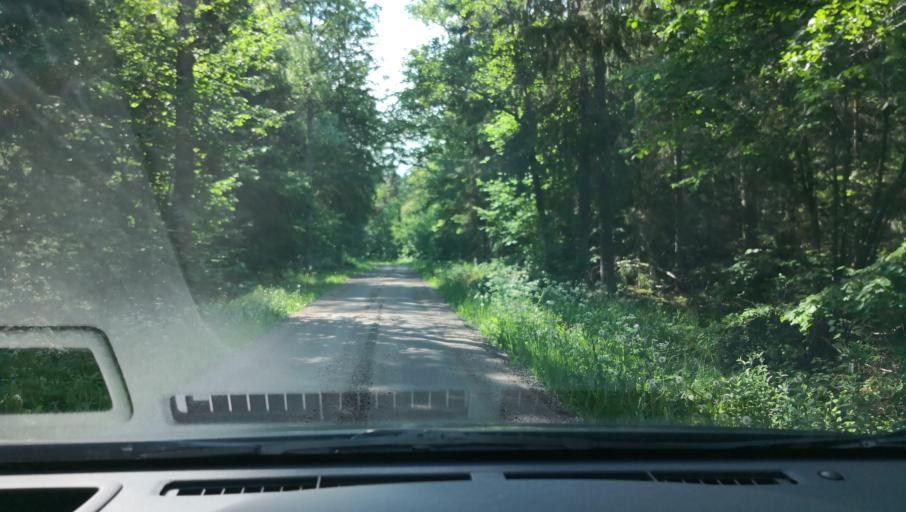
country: SE
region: Uppsala
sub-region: Enkopings Kommun
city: Orsundsbro
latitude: 59.8355
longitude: 17.2302
